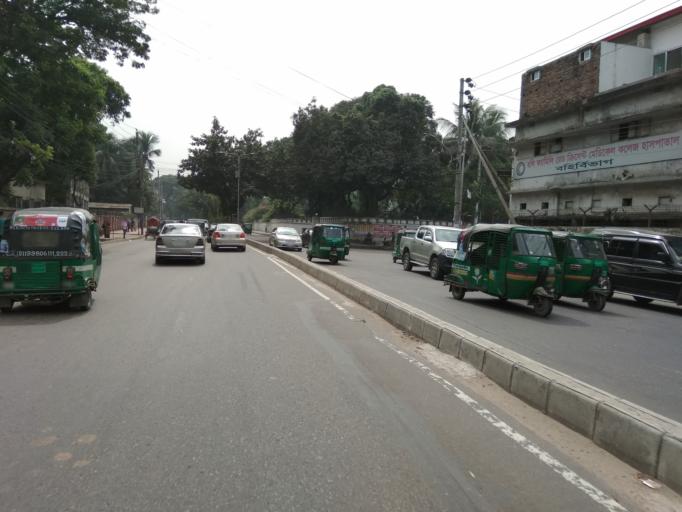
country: BD
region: Dhaka
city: Paltan
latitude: 23.7466
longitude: 90.4040
